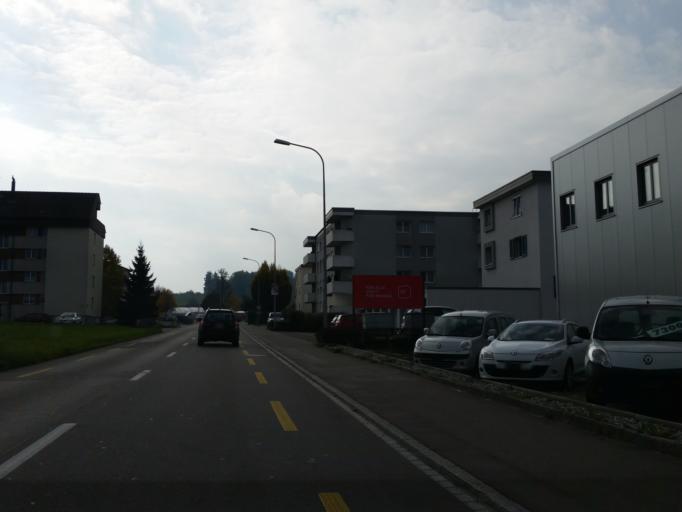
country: CH
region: Thurgau
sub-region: Arbon District
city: Amriswil
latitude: 47.5461
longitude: 9.2745
